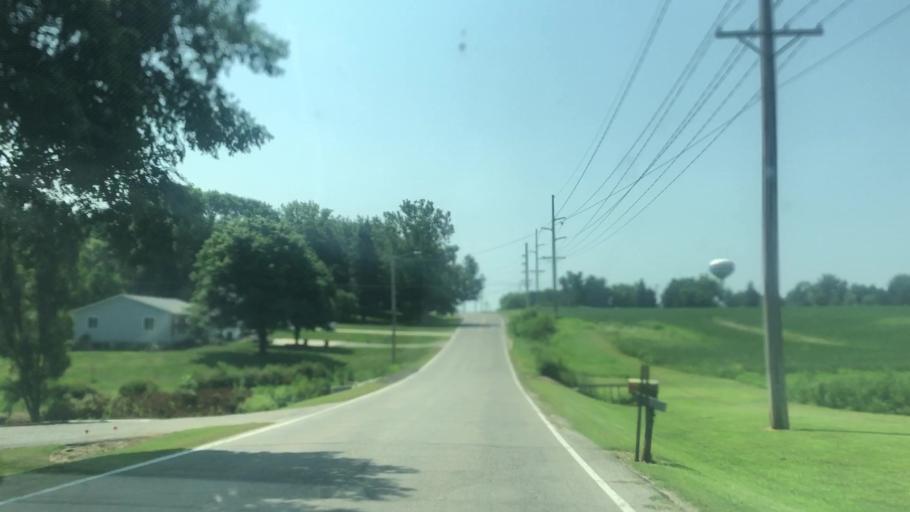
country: US
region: Iowa
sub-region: Marshall County
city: Marshalltown
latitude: 42.0356
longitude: -92.9608
